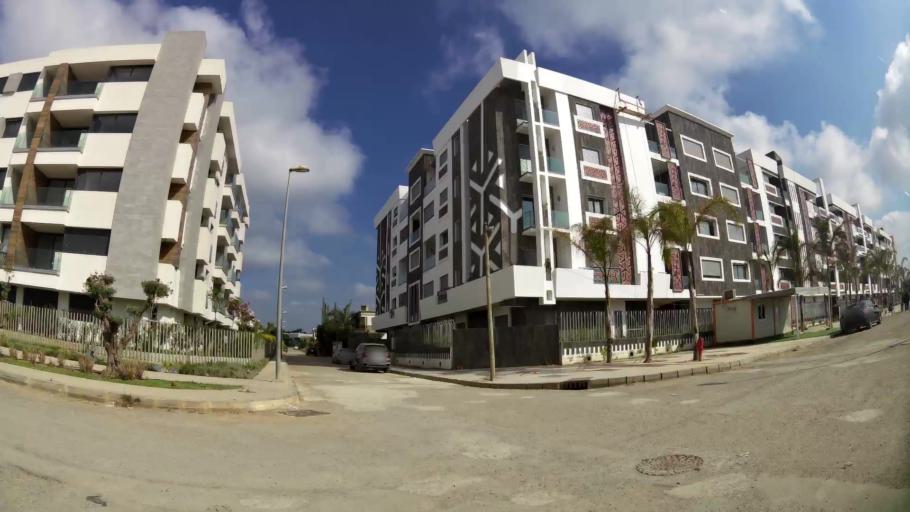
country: MA
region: Rabat-Sale-Zemmour-Zaer
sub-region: Skhirate-Temara
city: Temara
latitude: 33.9498
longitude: -6.8787
